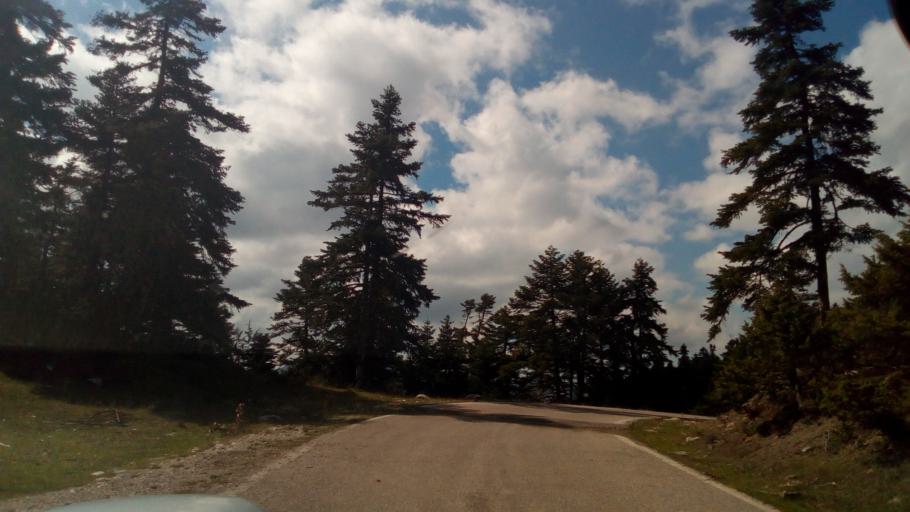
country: GR
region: West Greece
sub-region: Nomos Aitolias kai Akarnanias
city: Nafpaktos
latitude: 38.6398
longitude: 21.9399
